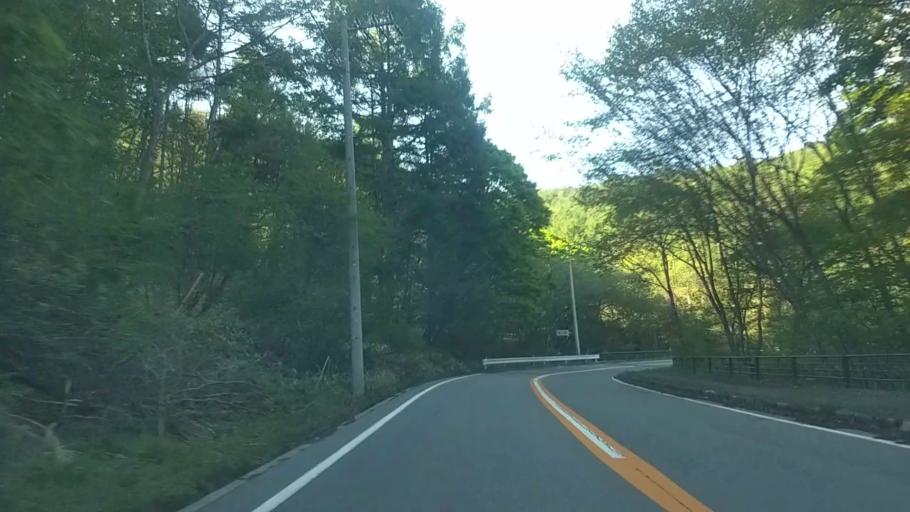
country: JP
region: Yamanashi
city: Nirasaki
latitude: 35.9071
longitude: 138.3846
